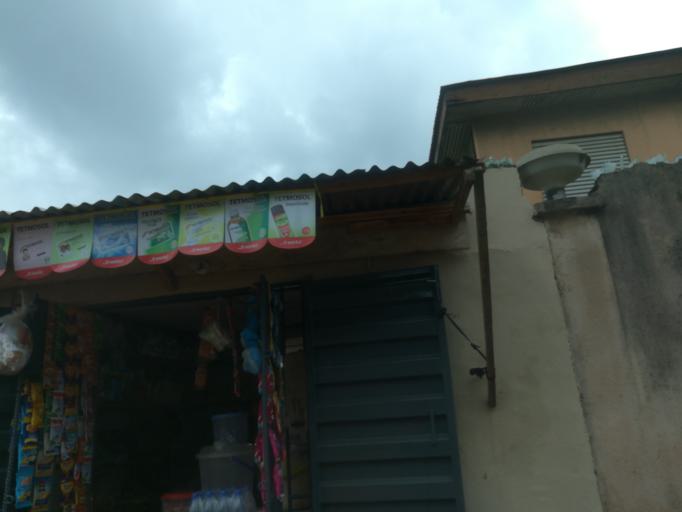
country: NG
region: Lagos
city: Oshodi
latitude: 6.5549
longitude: 3.3293
